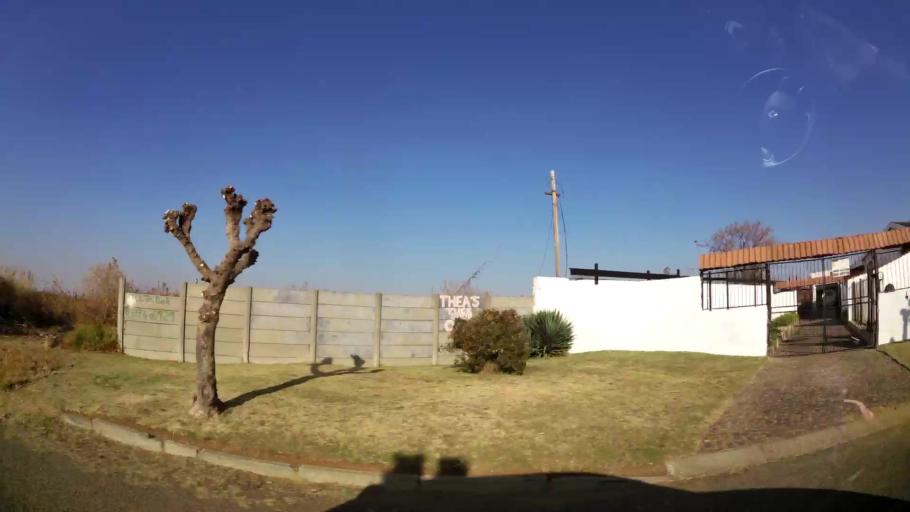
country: ZA
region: Gauteng
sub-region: West Rand District Municipality
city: Randfontein
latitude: -26.1963
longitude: 27.7013
